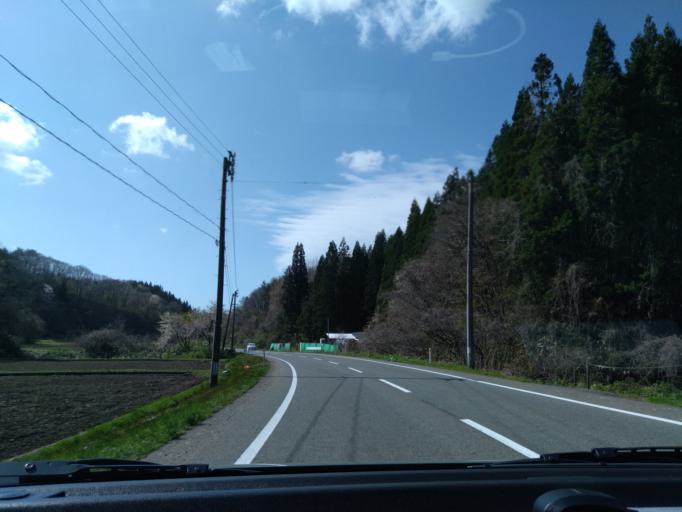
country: JP
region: Akita
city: Akita
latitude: 39.7044
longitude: 140.2137
